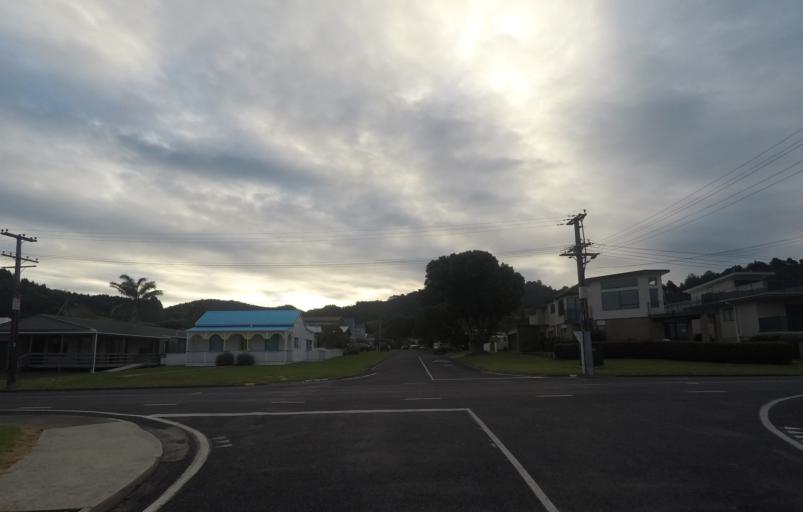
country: NZ
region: Bay of Plenty
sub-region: Western Bay of Plenty District
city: Waihi Beach
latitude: -37.3994
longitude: 175.9372
